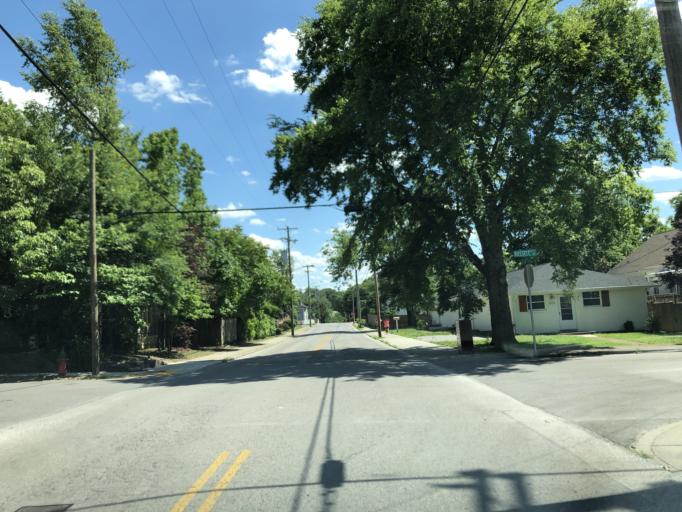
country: US
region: Tennessee
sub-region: Davidson County
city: Nashville
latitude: 36.1746
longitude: -86.7423
